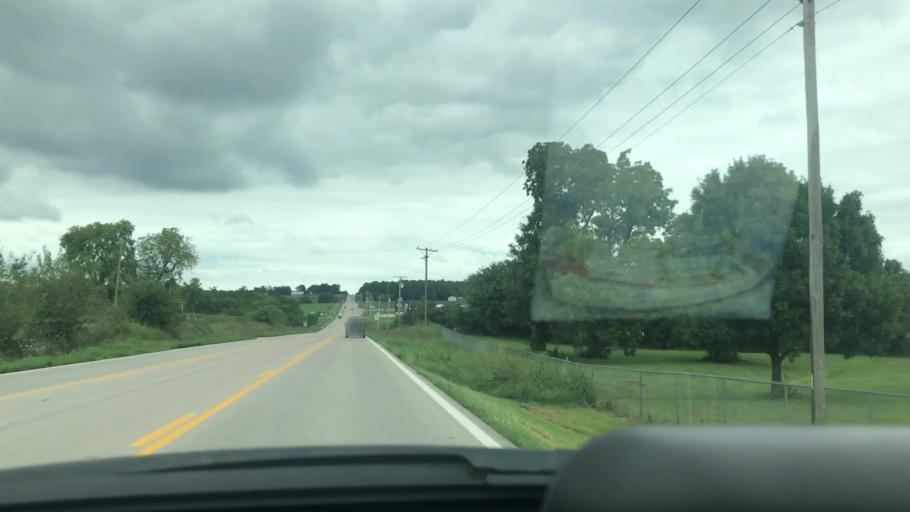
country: US
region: Missouri
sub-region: Dallas County
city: Buffalo
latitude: 37.6614
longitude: -93.1035
